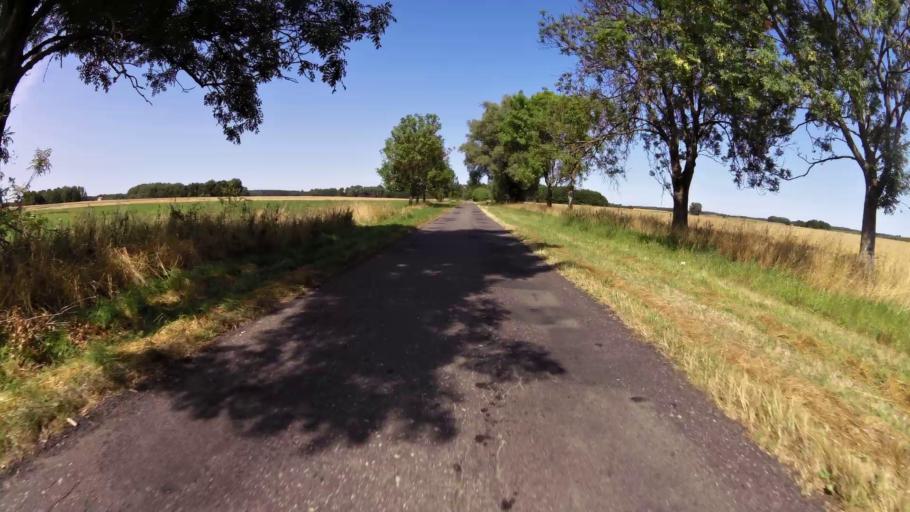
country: PL
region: West Pomeranian Voivodeship
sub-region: Powiat stargardzki
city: Suchan
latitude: 53.2825
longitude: 15.3624
